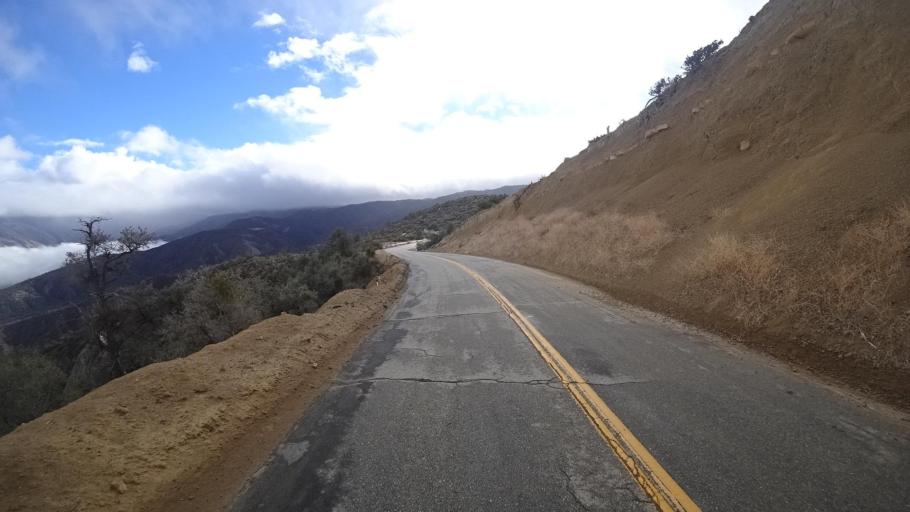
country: US
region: California
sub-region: Kern County
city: Maricopa
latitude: 34.8925
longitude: -119.3569
